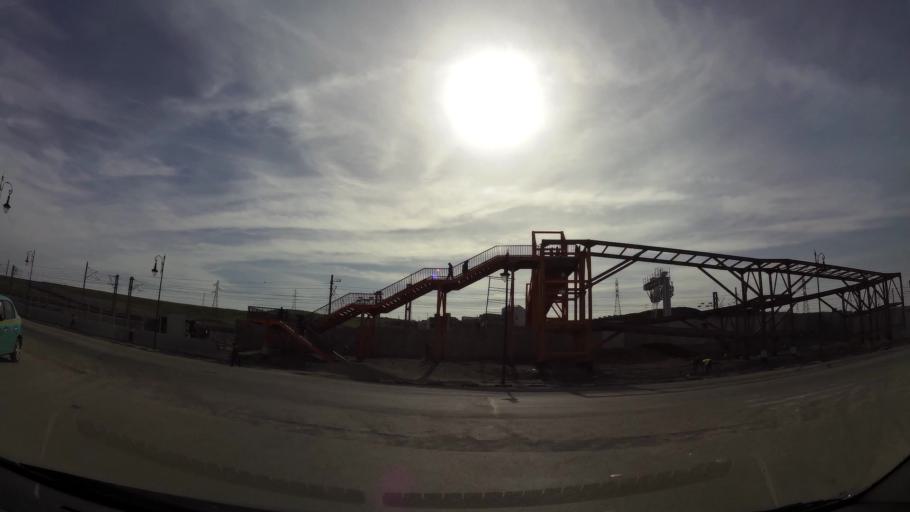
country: MA
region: Tanger-Tetouan
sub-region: Tanger-Assilah
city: Tangier
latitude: 35.7362
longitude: -5.7961
